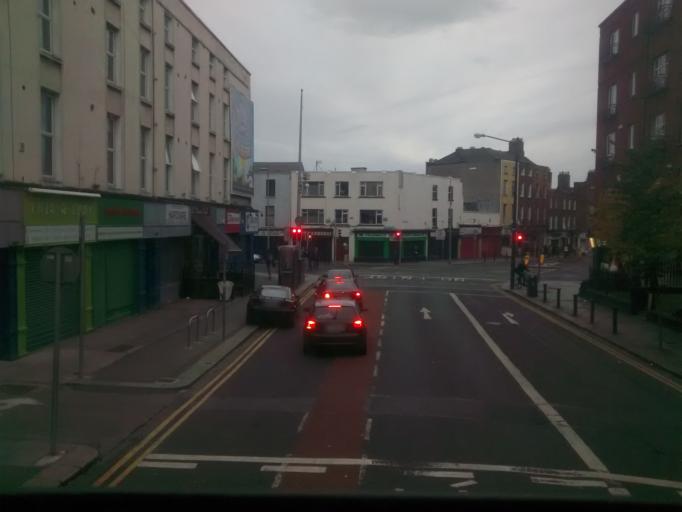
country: IE
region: Leinster
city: Drumcondra
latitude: 53.3563
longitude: -6.2659
